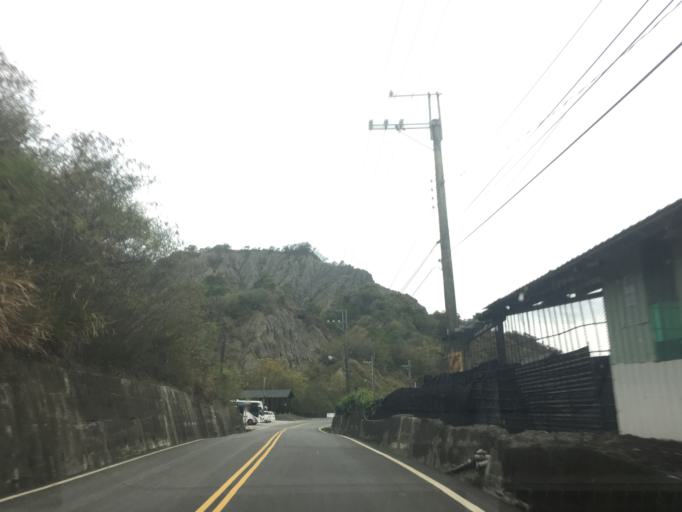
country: TW
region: Taiwan
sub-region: Taitung
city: Taitung
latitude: 22.8164
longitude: 121.1375
